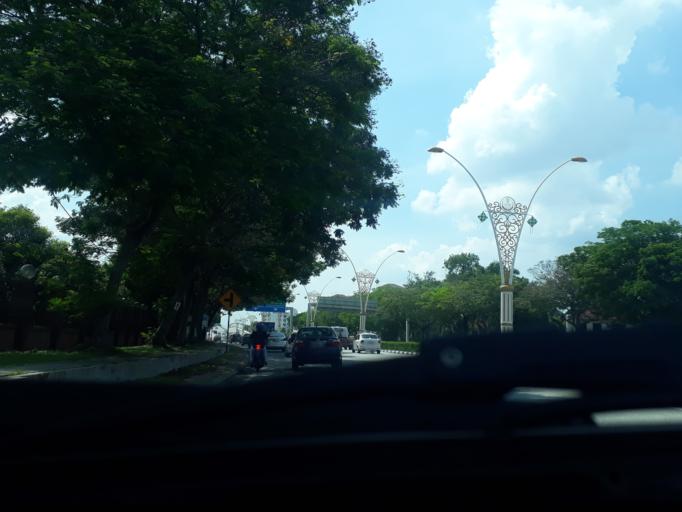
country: MY
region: Perak
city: Ipoh
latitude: 4.5968
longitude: 101.1201
